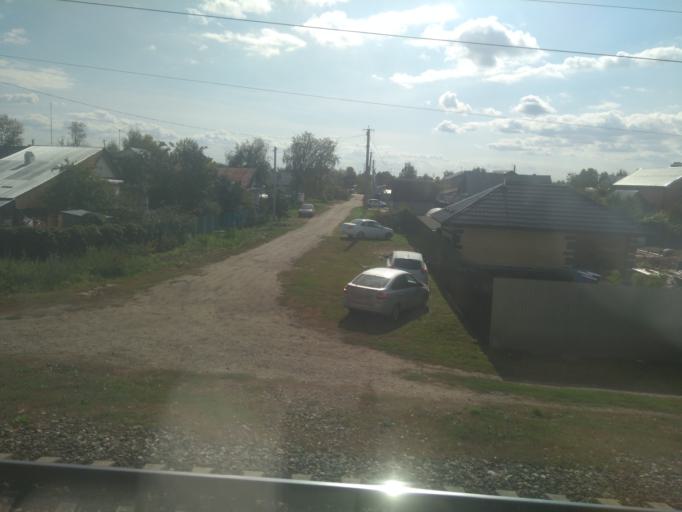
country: RU
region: Tatarstan
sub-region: Zelenodol'skiy Rayon
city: Zelenodolsk
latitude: 55.8419
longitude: 48.5704
